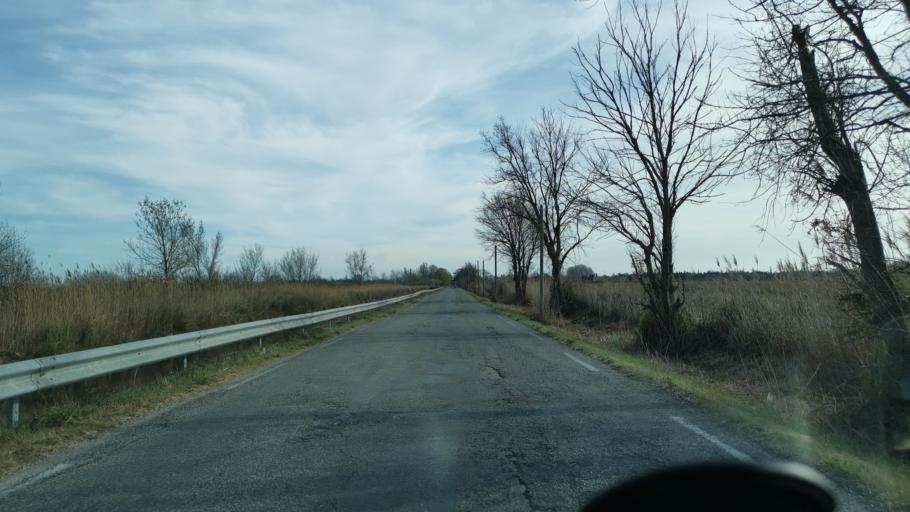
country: FR
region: Provence-Alpes-Cote d'Azur
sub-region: Departement des Bouches-du-Rhone
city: Arles
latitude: 43.6296
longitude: 4.7111
